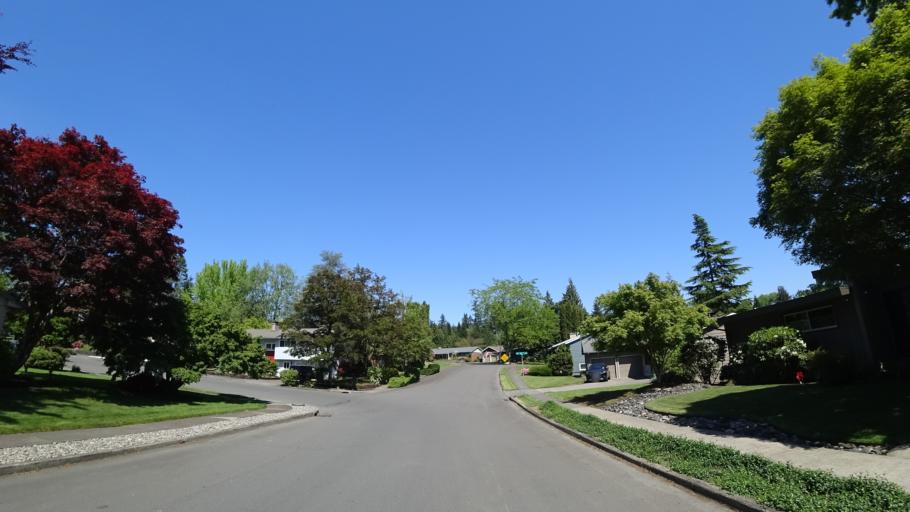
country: US
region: Oregon
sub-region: Washington County
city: Cedar Hills
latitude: 45.4976
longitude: -122.7934
